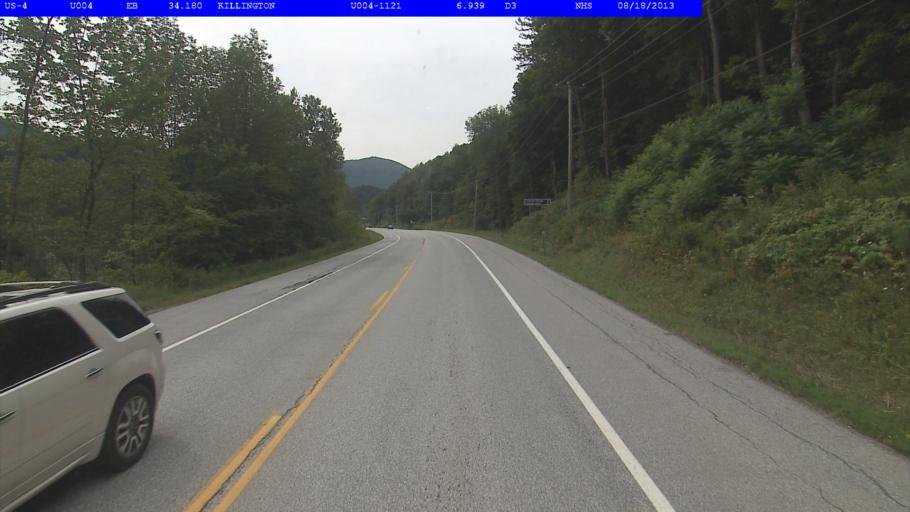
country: US
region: Vermont
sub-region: Rutland County
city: Rutland
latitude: 43.6209
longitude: -72.7598
